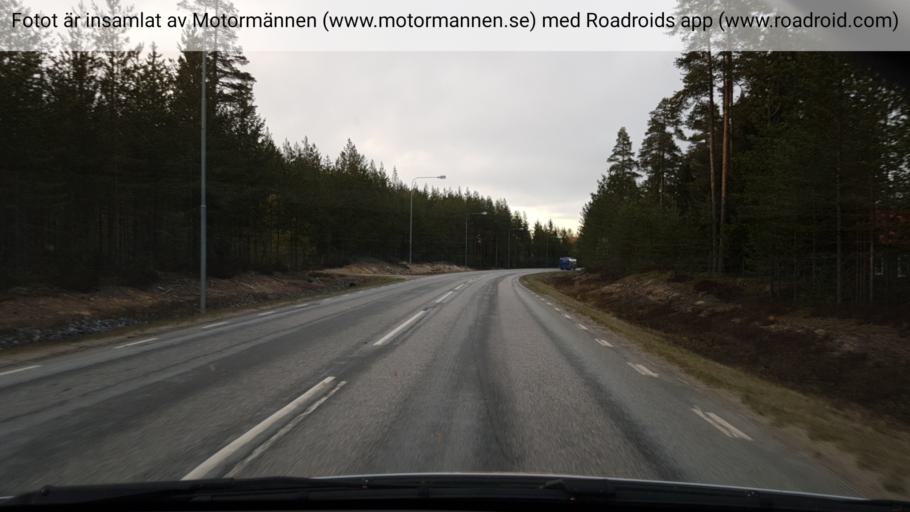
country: SE
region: Vaesterbotten
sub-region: Umea Kommun
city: Roback
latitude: 63.8069
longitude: 20.1692
